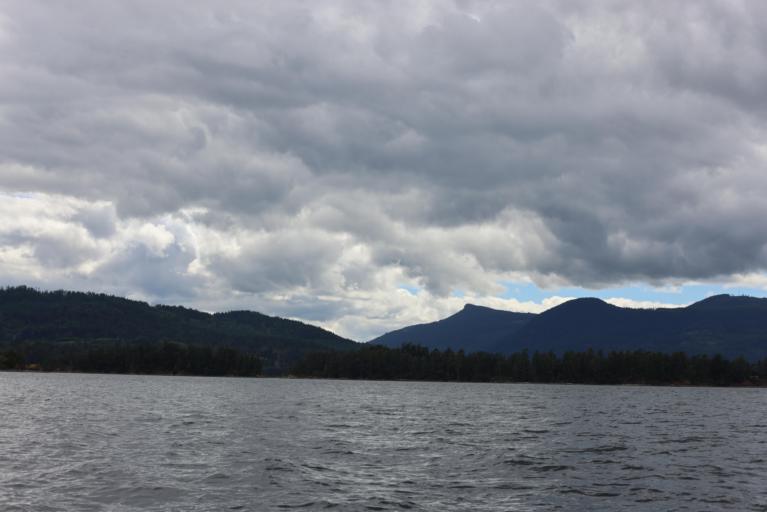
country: CA
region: British Columbia
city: North Cowichan
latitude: 48.8962
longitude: -123.6457
